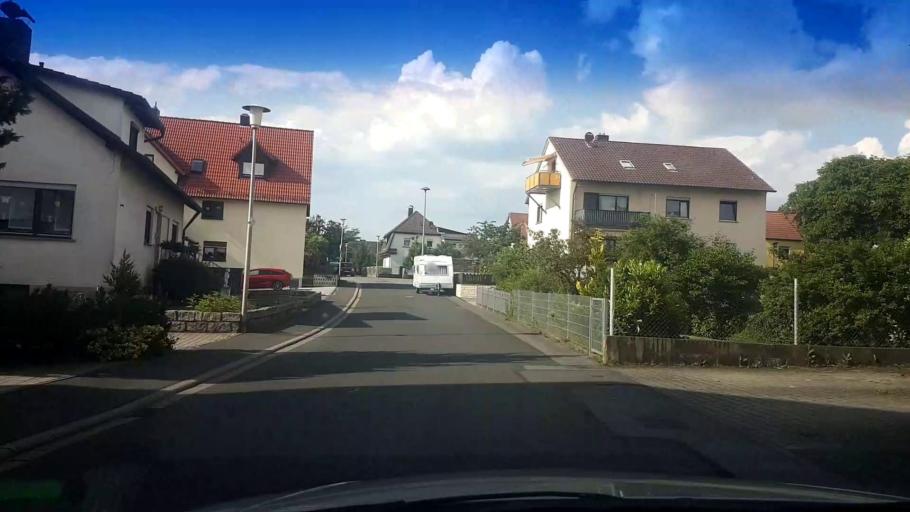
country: DE
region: Bavaria
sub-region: Upper Franconia
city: Breitengussbach
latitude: 49.9671
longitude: 10.8835
